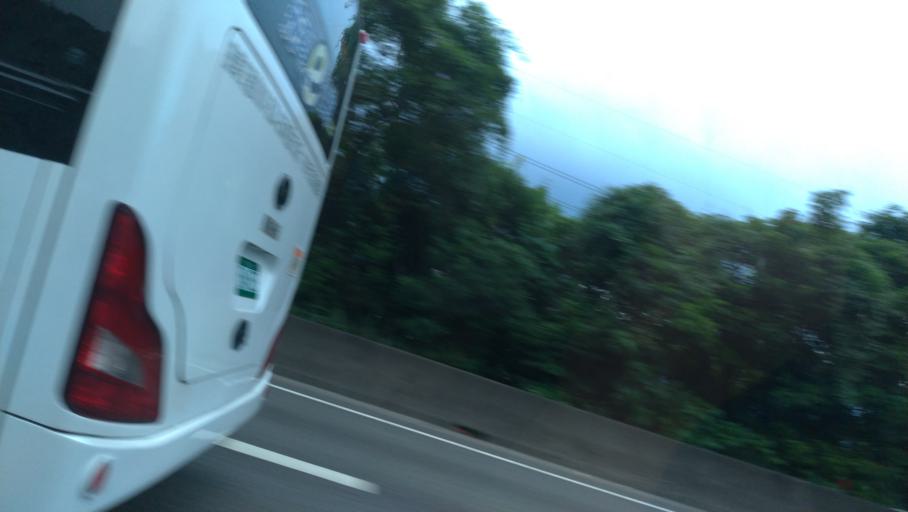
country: TW
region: Taiwan
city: Daxi
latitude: 24.9183
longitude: 121.2963
